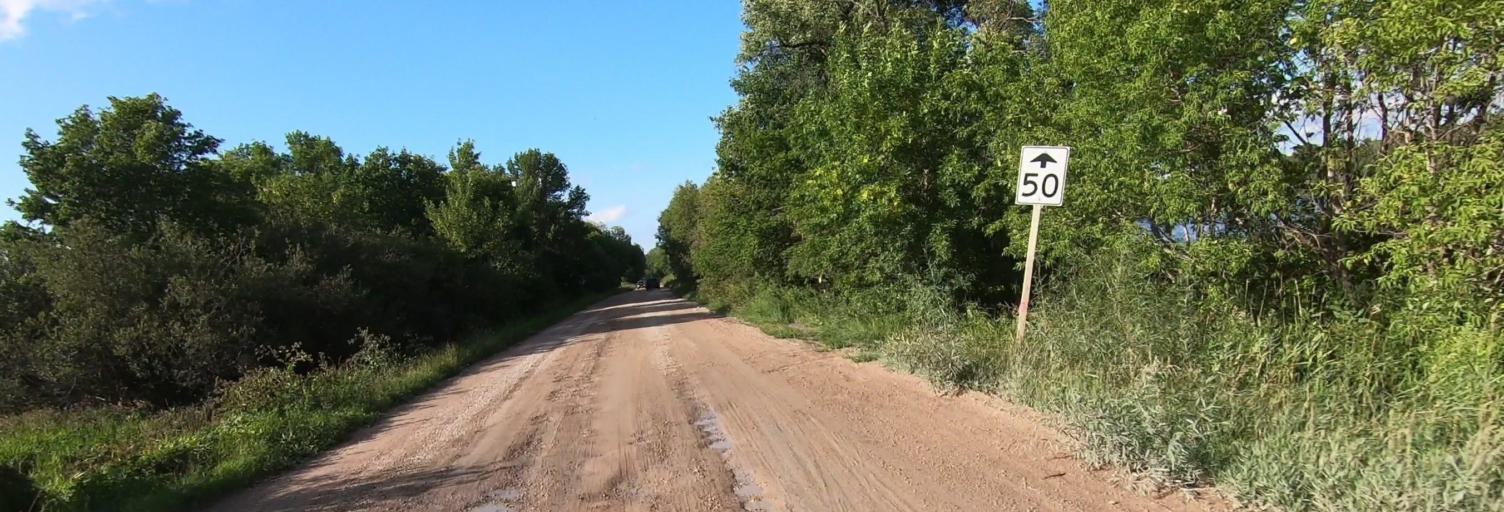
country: CA
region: Manitoba
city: Selkirk
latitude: 50.2620
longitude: -96.8497
